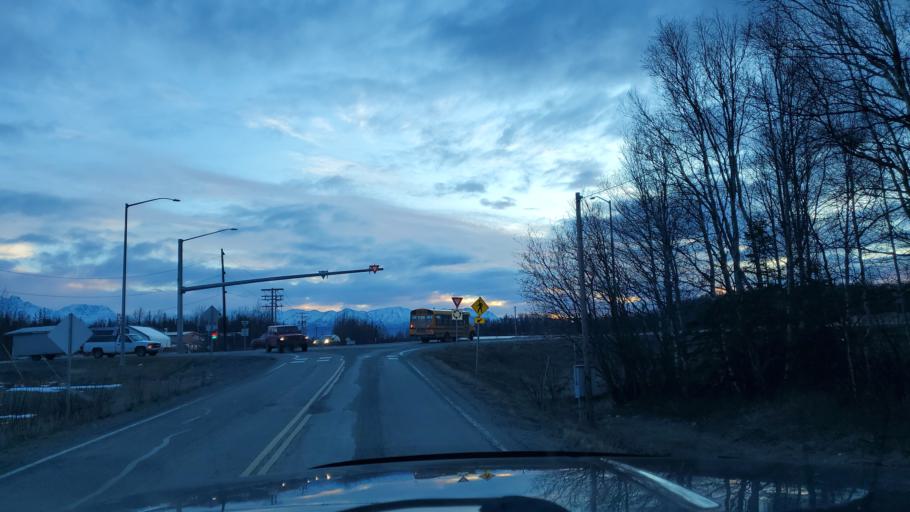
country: US
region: Alaska
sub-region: Matanuska-Susitna Borough
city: Lakes
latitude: 61.6145
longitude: -149.3301
